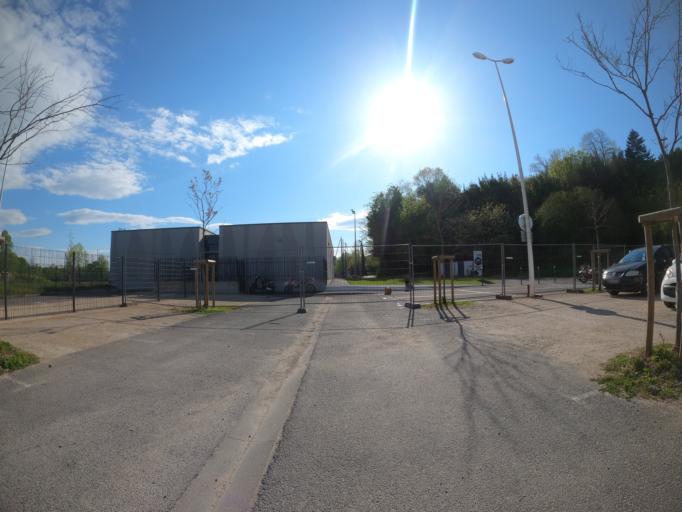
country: FR
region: Aquitaine
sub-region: Departement des Pyrenees-Atlantiques
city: Bayonne
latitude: 43.4781
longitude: -1.4747
